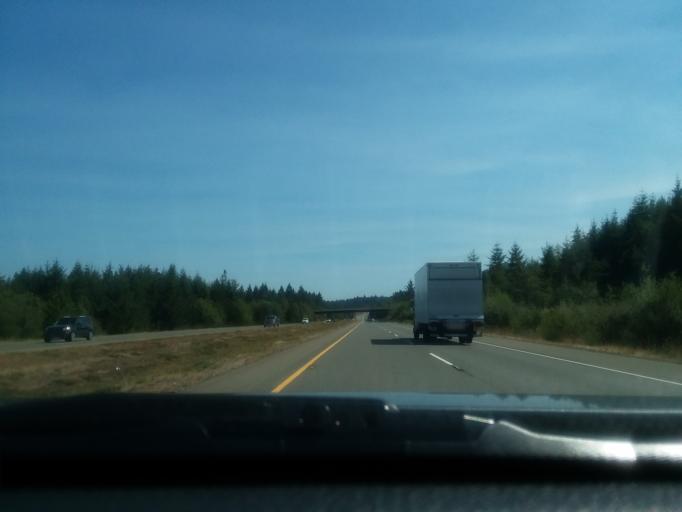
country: CA
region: British Columbia
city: Port Alberni
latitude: 49.3927
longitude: -124.6449
